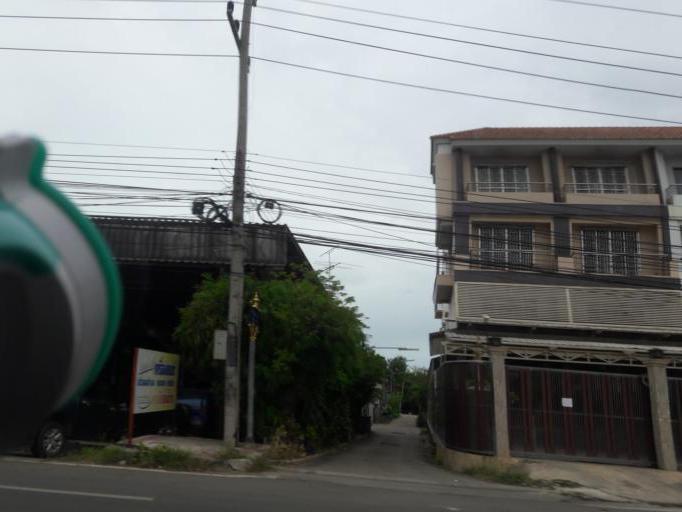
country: TH
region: Ratchaburi
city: Damnoen Saduak
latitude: 13.5543
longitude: 99.9681
